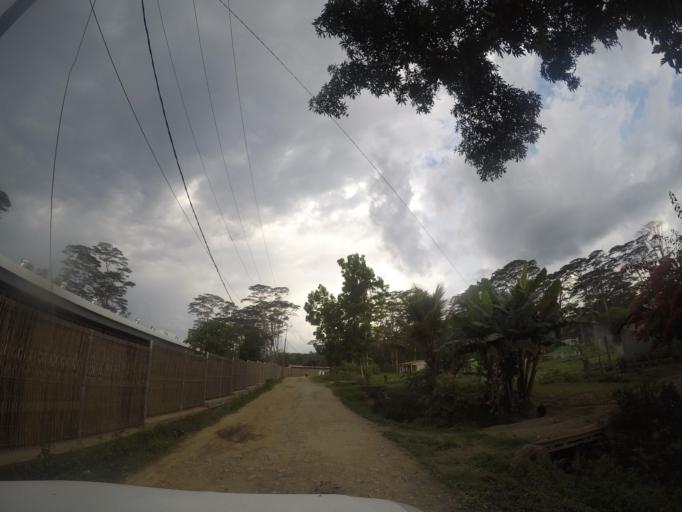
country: TL
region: Ermera
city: Gleno
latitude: -8.7249
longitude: 125.4415
